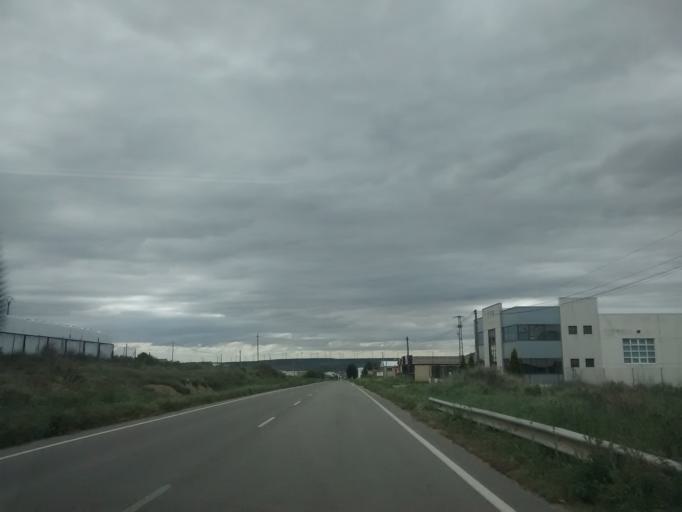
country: ES
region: La Rioja
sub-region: Provincia de La Rioja
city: Pradejon
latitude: 42.3428
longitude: -2.0854
